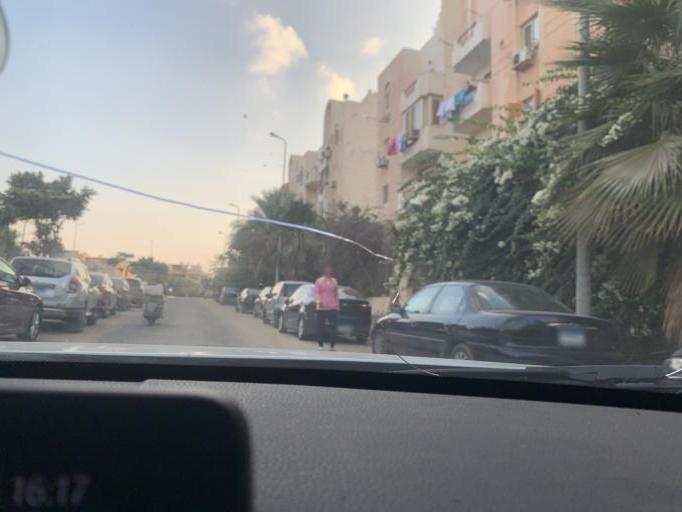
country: EG
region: Muhafazat al Qalyubiyah
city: Al Khankah
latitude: 30.0178
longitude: 31.4807
